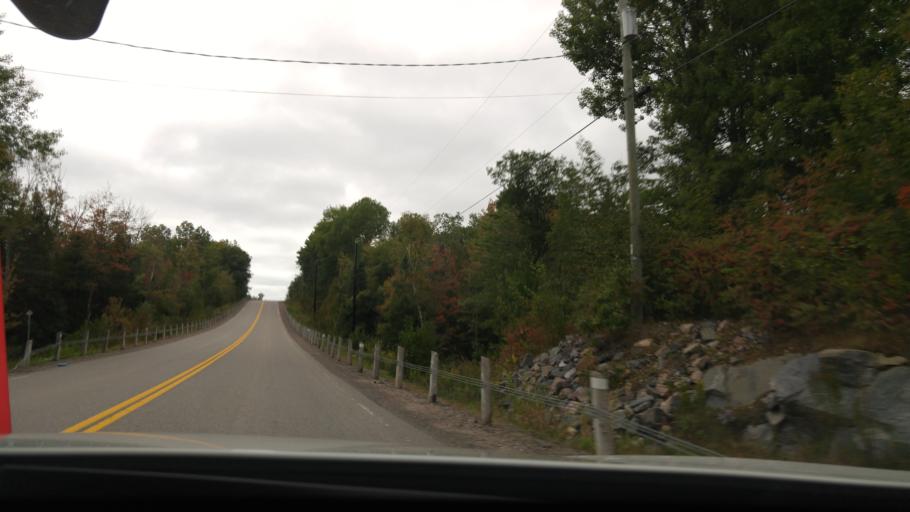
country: CA
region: Ontario
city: Petawawa
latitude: 45.8258
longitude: -77.2862
